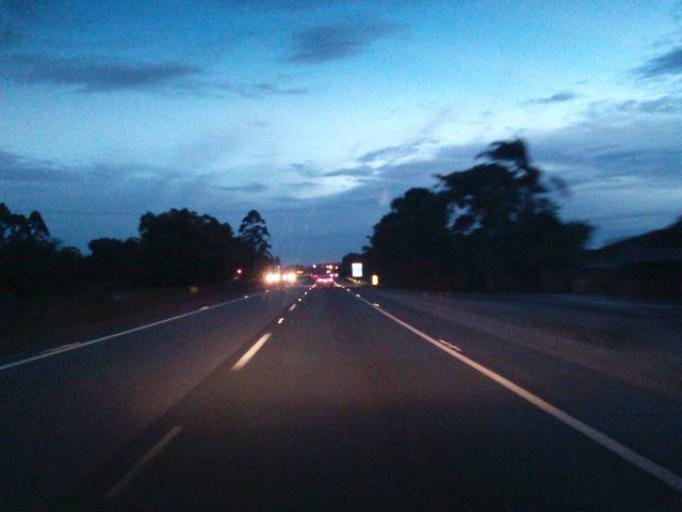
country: BR
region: Santa Catarina
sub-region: Barra Velha
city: Barra Velha
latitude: -26.5814
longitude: -48.7223
